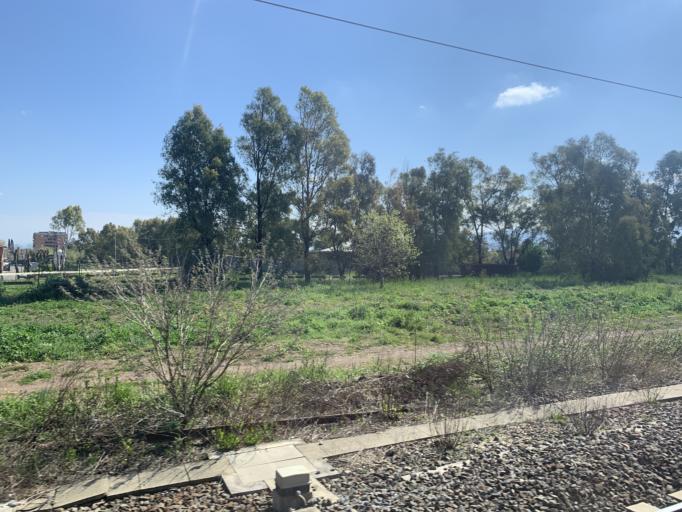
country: IT
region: Latium
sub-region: Citta metropolitana di Roma Capitale
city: Ciampino
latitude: 41.8283
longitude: 12.5707
